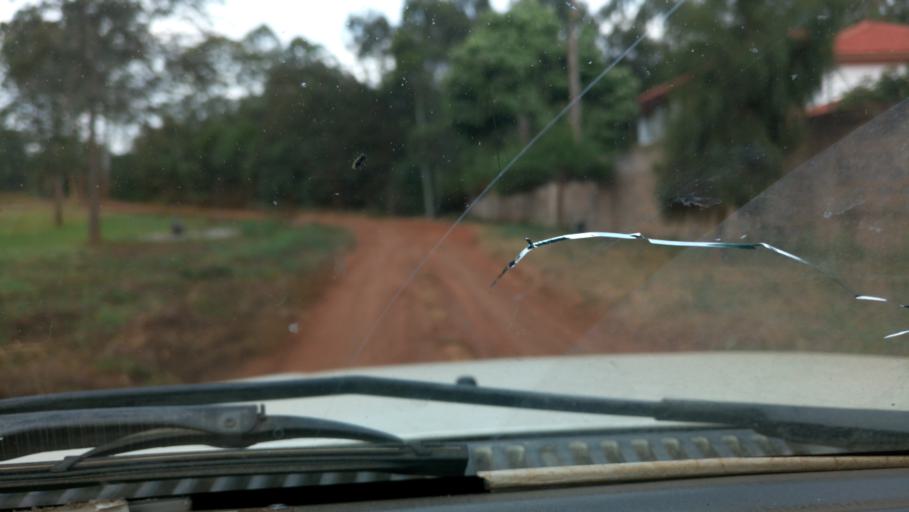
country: KE
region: Kajiado
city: Ngong
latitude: -1.3333
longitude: 36.7208
